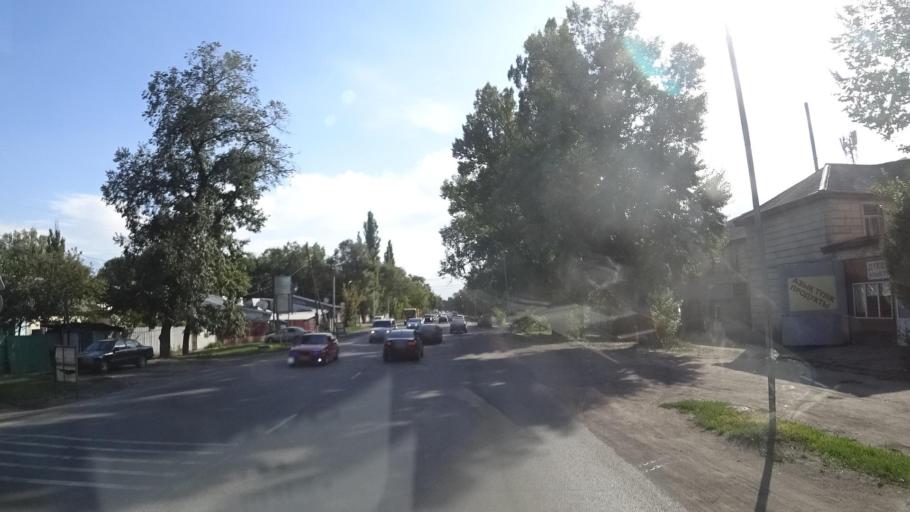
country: KZ
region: Almaty Oblysy
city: Energeticheskiy
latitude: 43.3842
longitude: 76.9996
